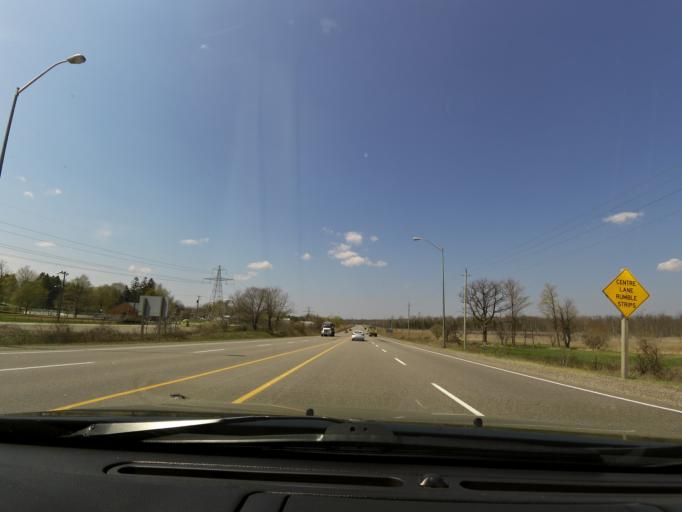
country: CA
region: Ontario
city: Ancaster
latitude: 43.4025
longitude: -80.0392
